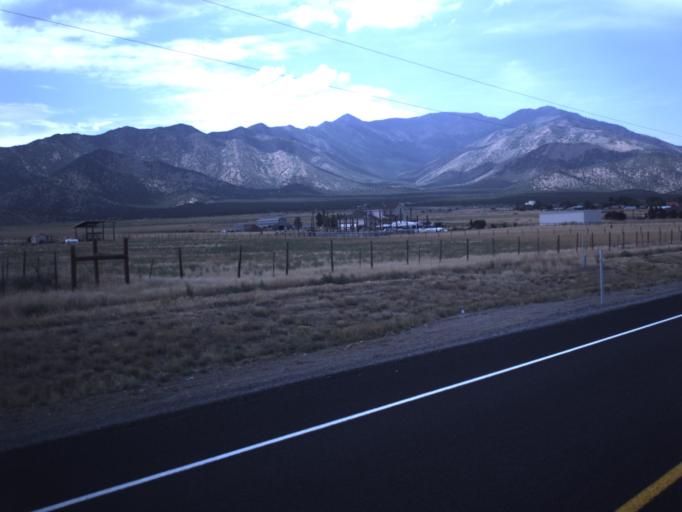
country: US
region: Utah
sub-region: Utah County
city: Eagle Mountain
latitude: 40.2882
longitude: -112.0971
